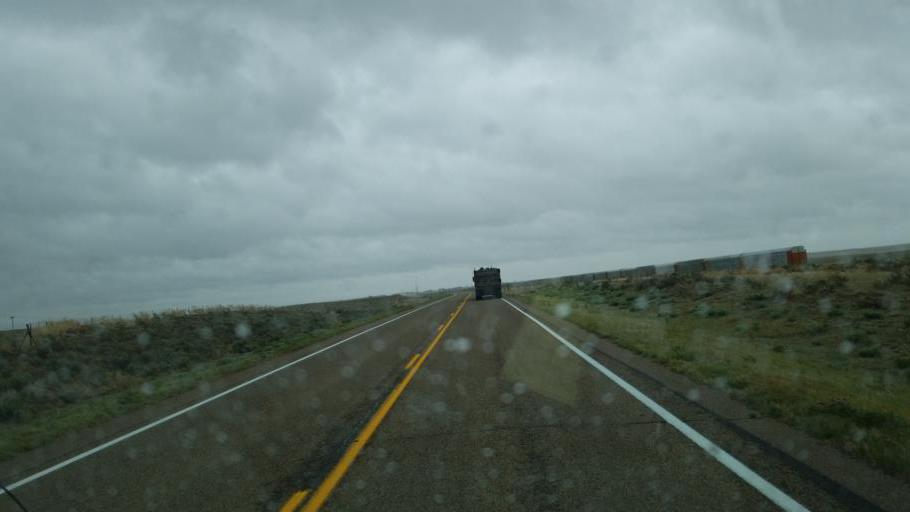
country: US
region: Colorado
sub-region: Kiowa County
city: Eads
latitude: 38.7739
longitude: -102.7496
